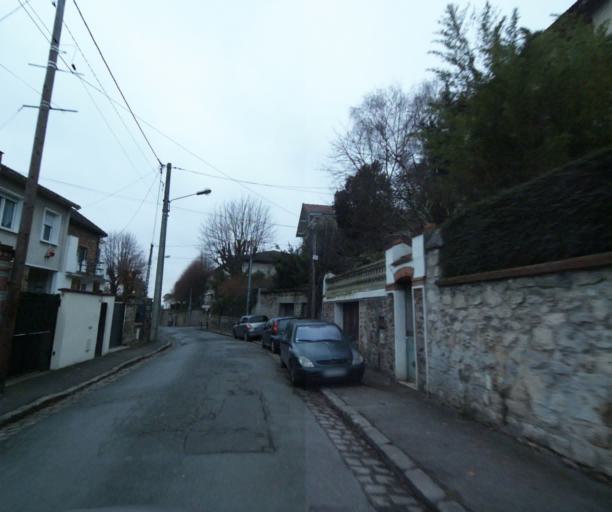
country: FR
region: Ile-de-France
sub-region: Departement du Val-de-Marne
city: Ablon-sur-Seine
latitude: 48.7270
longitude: 2.4153
